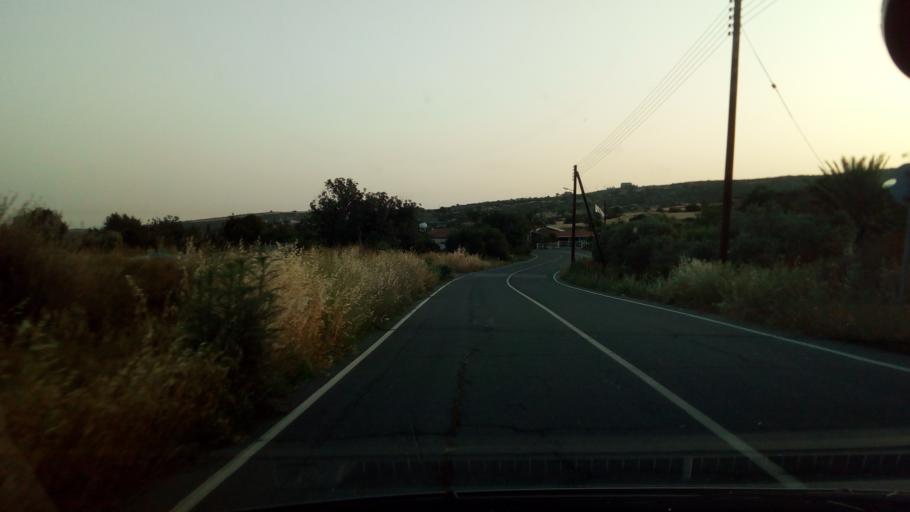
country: CY
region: Larnaka
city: Kofinou
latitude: 34.7880
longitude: 33.3286
